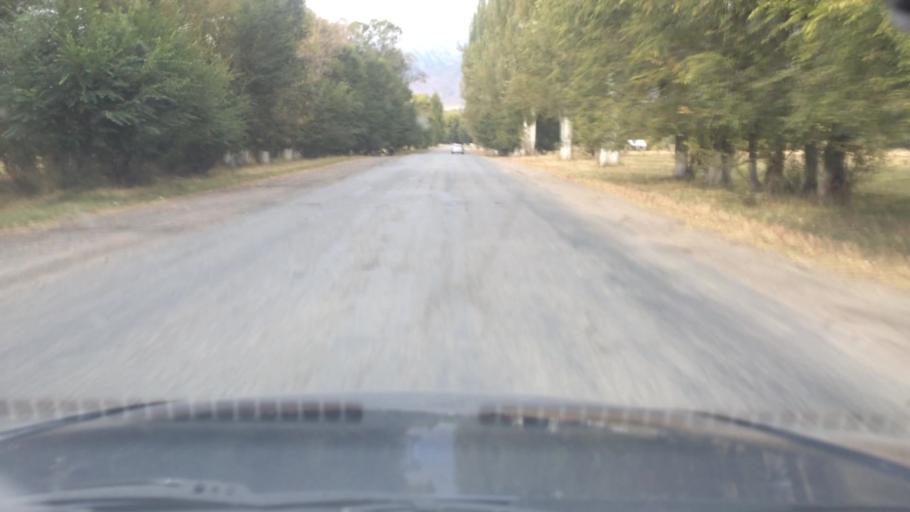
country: KG
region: Ysyk-Koel
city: Tyup
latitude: 42.7857
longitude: 78.2693
